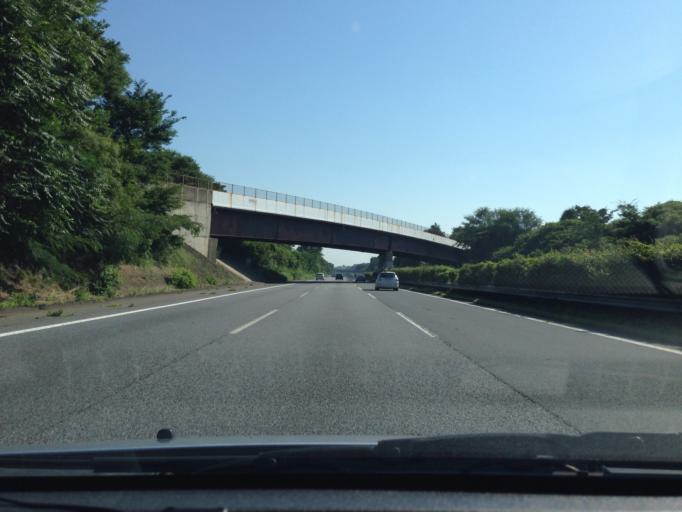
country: JP
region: Ibaraki
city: Ishioka
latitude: 36.1601
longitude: 140.2292
